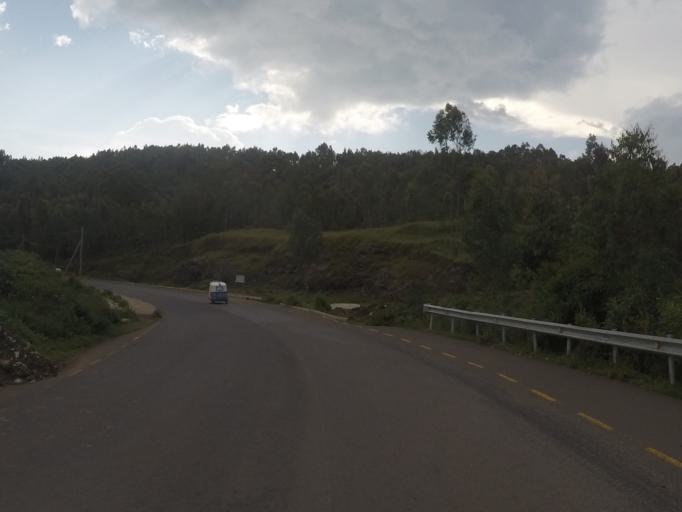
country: ET
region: Amhara
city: Gondar
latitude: 12.6322
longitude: 37.4717
